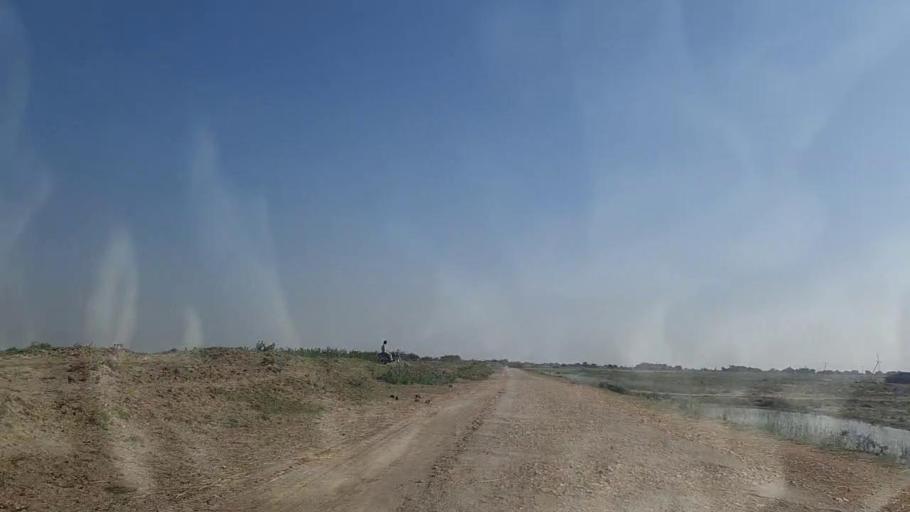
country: PK
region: Sindh
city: Mirpur Batoro
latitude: 24.6096
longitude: 68.1697
